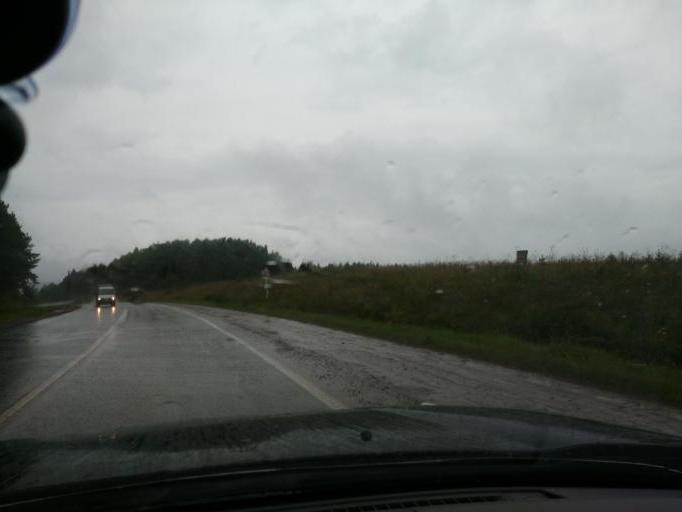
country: RU
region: Perm
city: Osa
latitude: 57.3238
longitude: 55.6128
